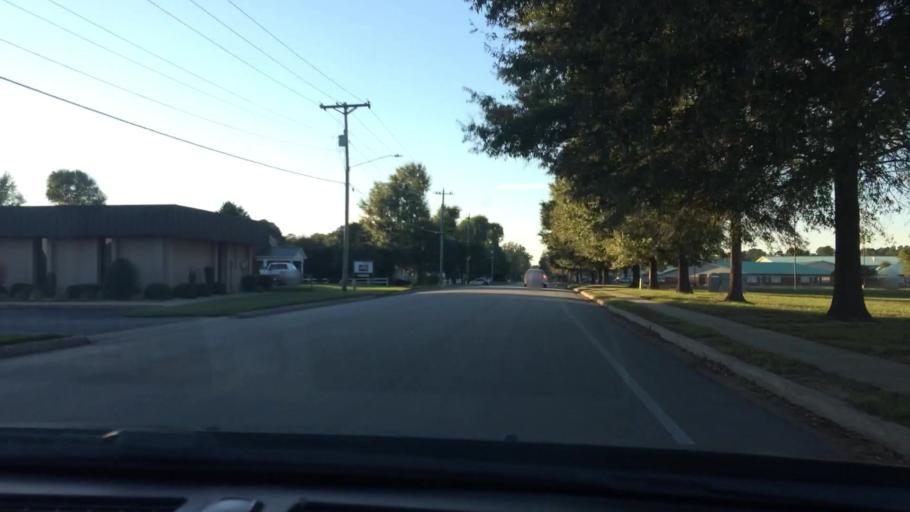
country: US
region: North Carolina
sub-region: Pitt County
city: Farmville
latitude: 35.5924
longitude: -77.5728
